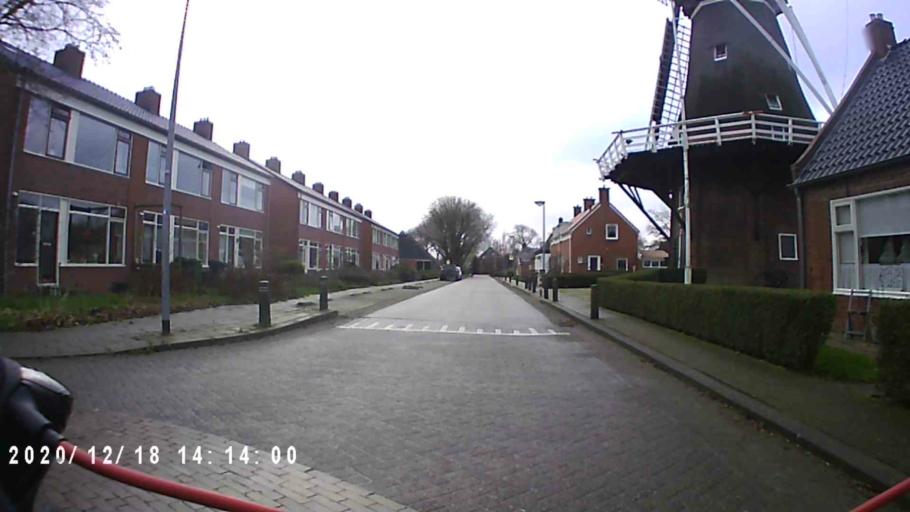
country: NL
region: Groningen
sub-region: Gemeente Bedum
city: Bedum
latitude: 53.2693
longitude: 6.6532
